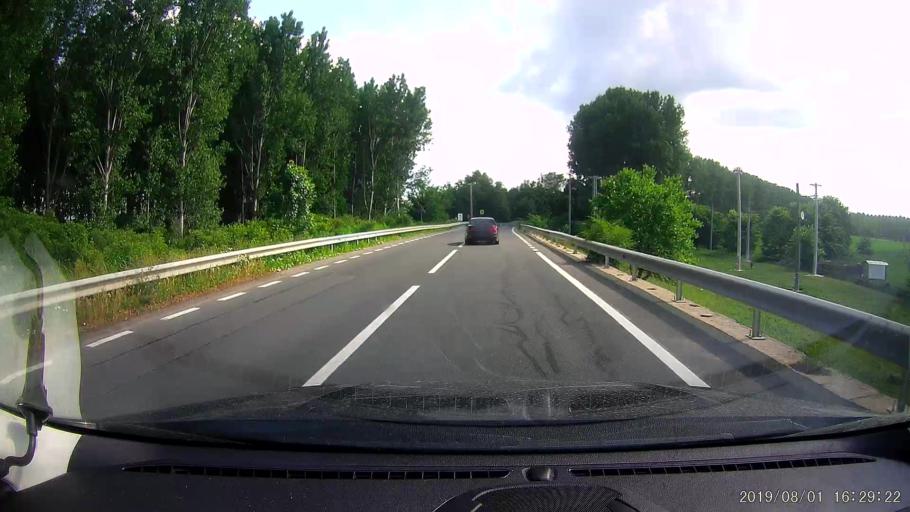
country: BG
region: Silistra
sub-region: Obshtina Silistra
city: Silistra
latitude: 44.1420
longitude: 27.2904
